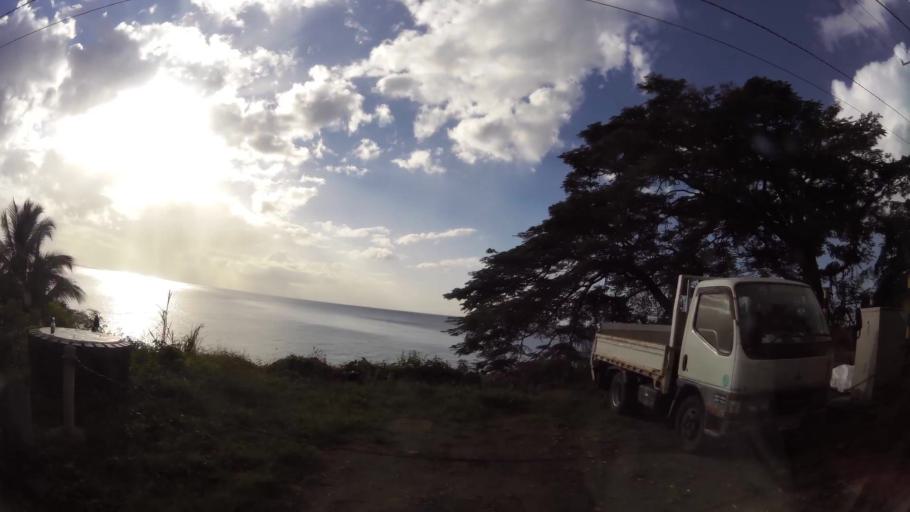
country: DM
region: Saint Paul
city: Mahaut
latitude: 15.3482
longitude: -61.3934
